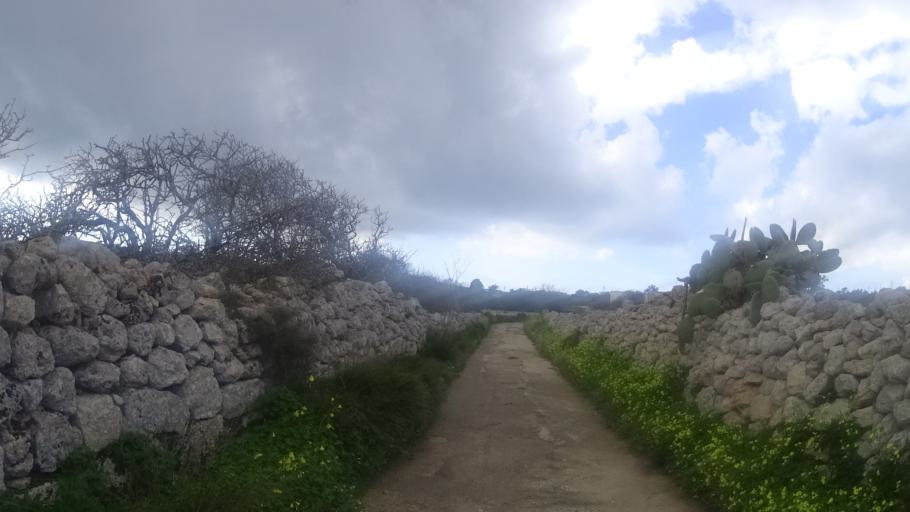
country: MT
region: L-Imgarr
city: Imgarr
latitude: 35.8953
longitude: 14.3719
